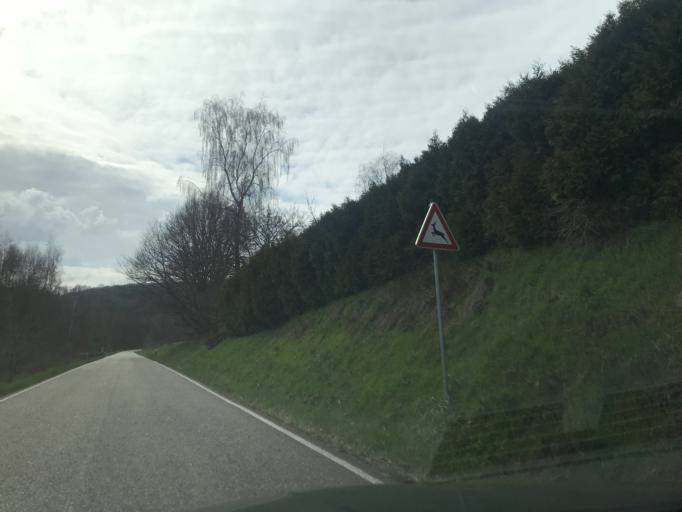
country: DE
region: Saarland
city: Blieskastel
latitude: 49.2092
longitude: 7.2463
